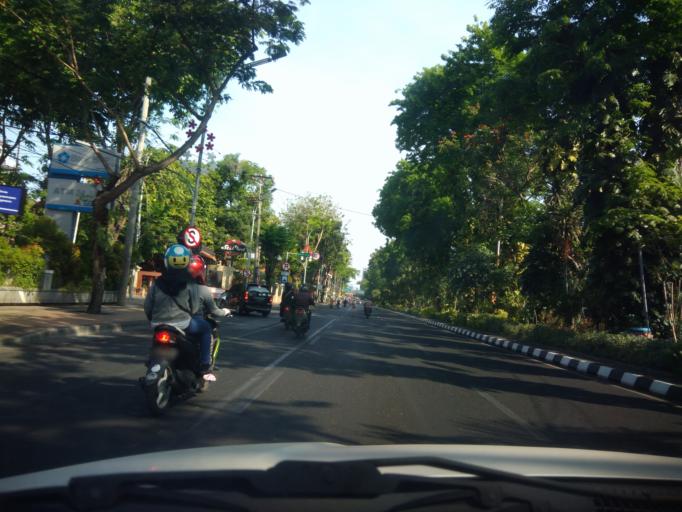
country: ID
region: East Java
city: Jagirsidosermo
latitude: -7.2925
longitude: 112.7391
